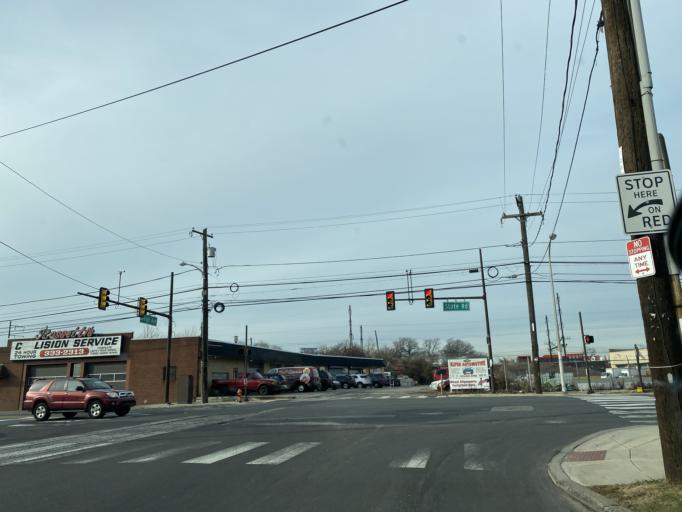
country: US
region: New Jersey
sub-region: Burlington County
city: Palmyra
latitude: 40.0272
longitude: -75.0286
